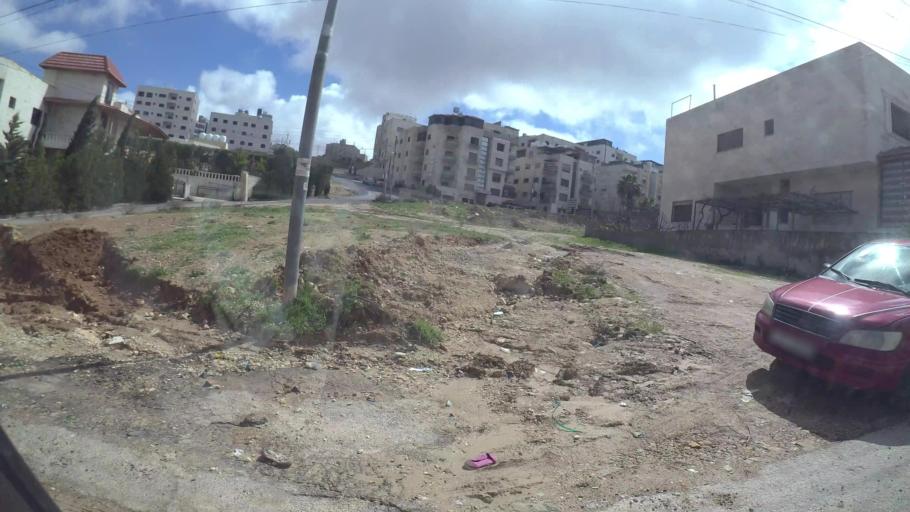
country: JO
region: Amman
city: Al Jubayhah
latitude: 32.0655
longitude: 35.8741
